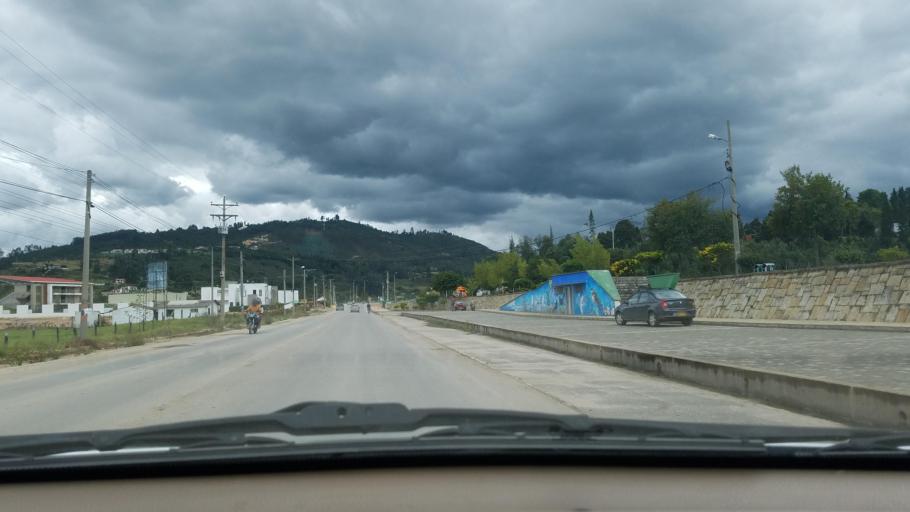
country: CO
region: Boyaca
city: Paipa
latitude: 5.7663
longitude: -73.1119
